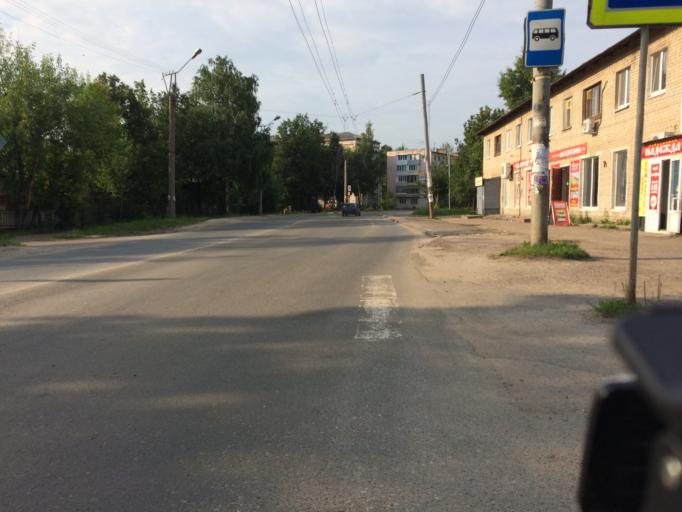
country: RU
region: Mariy-El
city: Yoshkar-Ola
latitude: 56.6287
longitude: 47.9473
